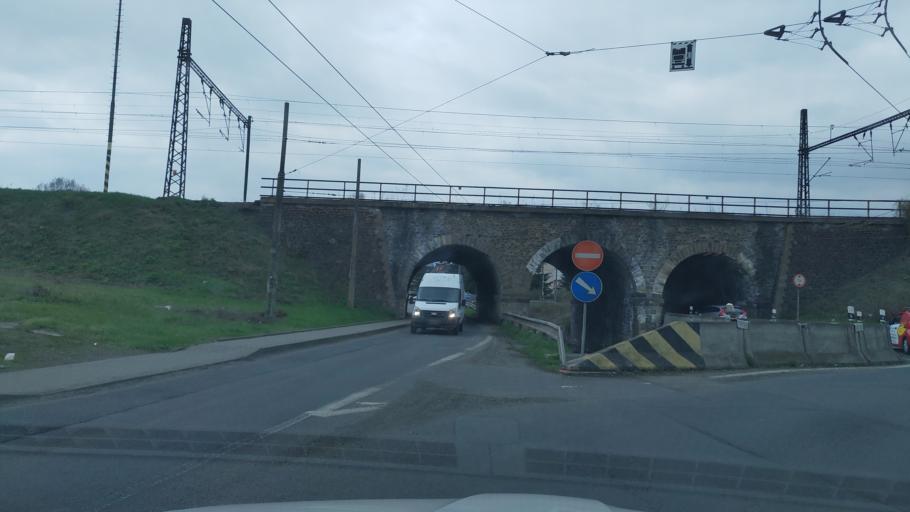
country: CZ
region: Ustecky
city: Trmice
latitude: 50.6531
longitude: 14.0015
